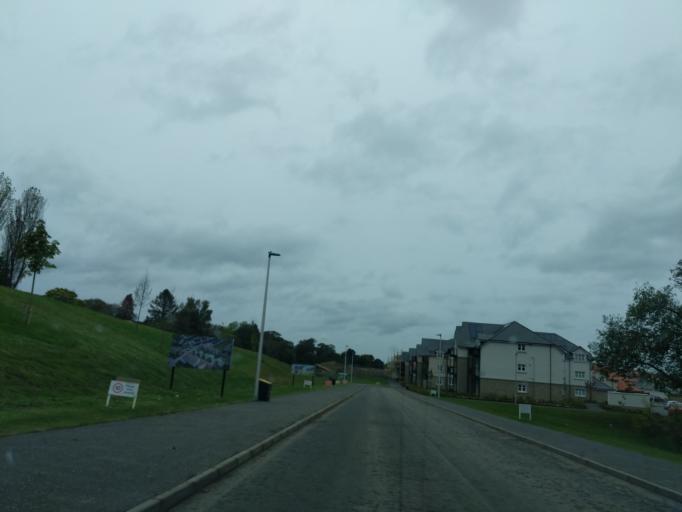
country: GB
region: Scotland
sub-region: Edinburgh
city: Balerno
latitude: 55.8900
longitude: -3.3355
